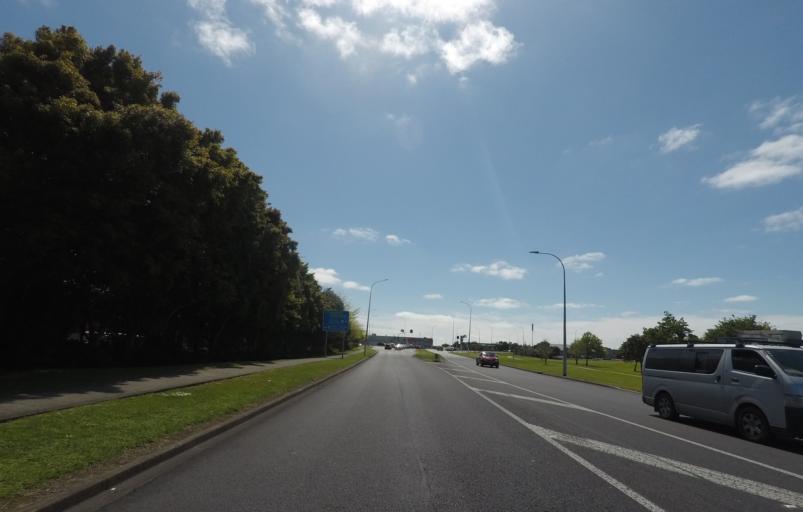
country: NZ
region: Auckland
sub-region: Auckland
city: Pakuranga
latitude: -36.9311
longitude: 174.9156
